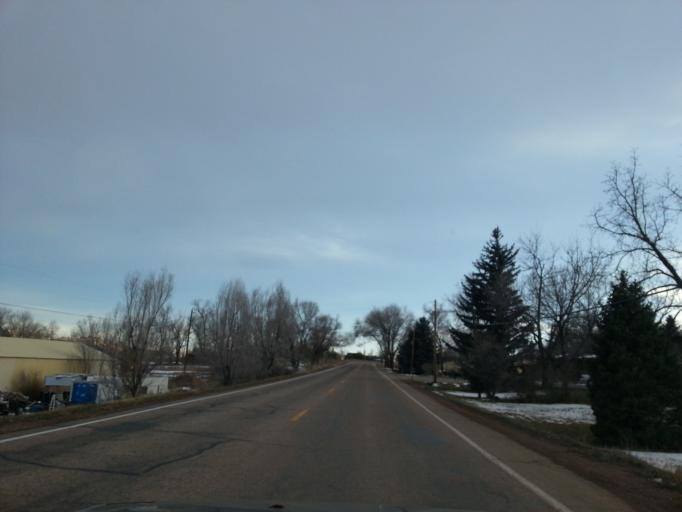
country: US
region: Colorado
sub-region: Larimer County
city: Loveland
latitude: 40.4317
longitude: -105.1944
